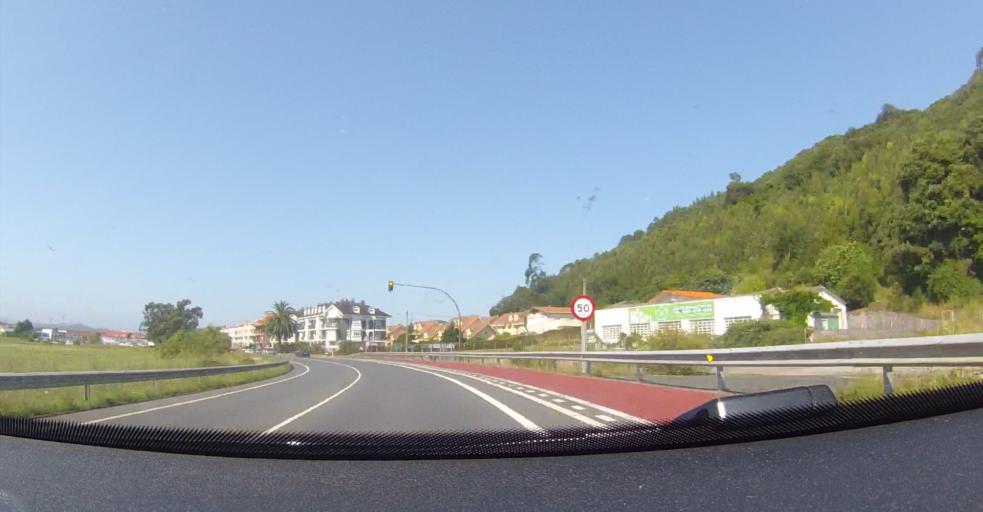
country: ES
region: Cantabria
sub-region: Provincia de Cantabria
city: Argonos
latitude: 43.4599
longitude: -3.4824
